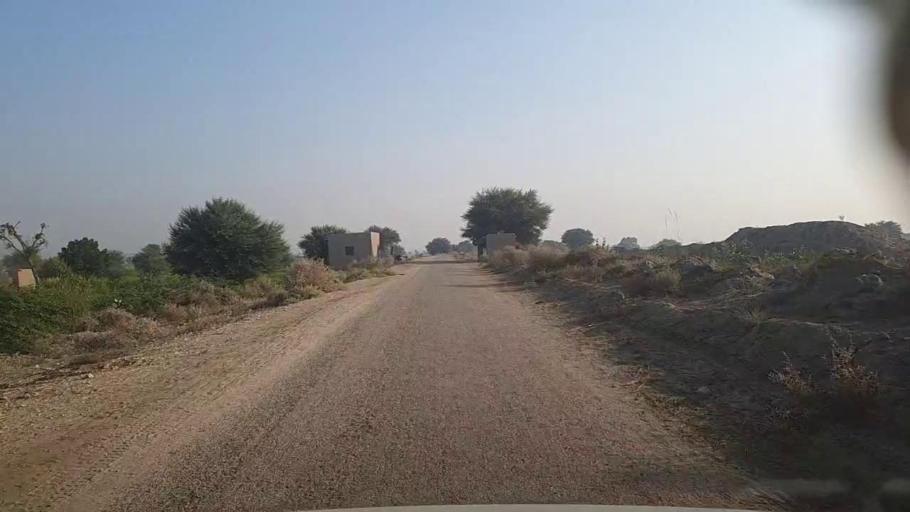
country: PK
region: Sindh
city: Karaundi
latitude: 26.7316
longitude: 68.4853
